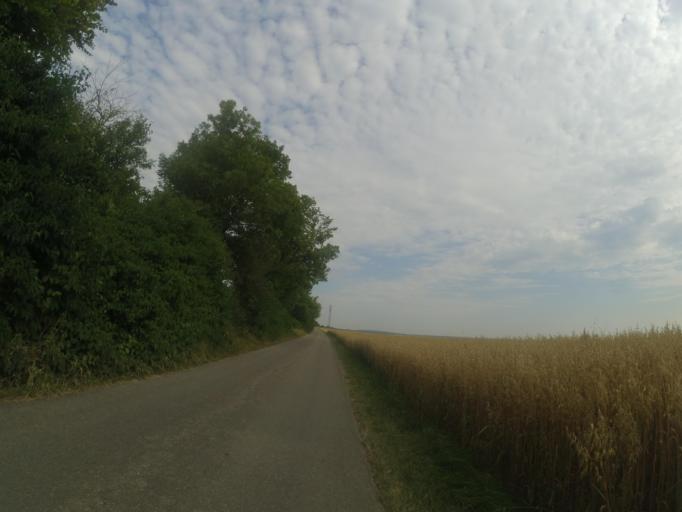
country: DE
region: Baden-Wuerttemberg
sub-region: Tuebingen Region
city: Dornstadt
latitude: 48.4885
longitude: 9.9317
